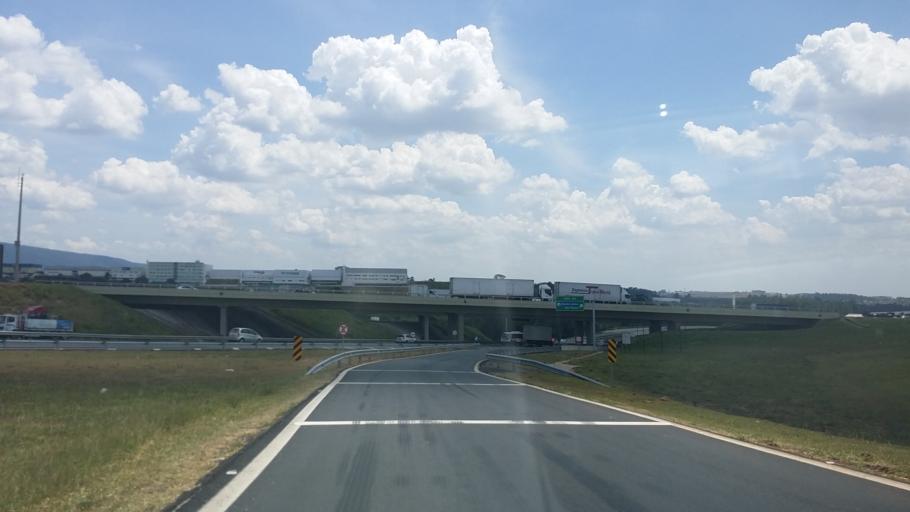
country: BR
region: Sao Paulo
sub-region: Jundiai
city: Jundiai
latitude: -23.1718
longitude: -46.9369
